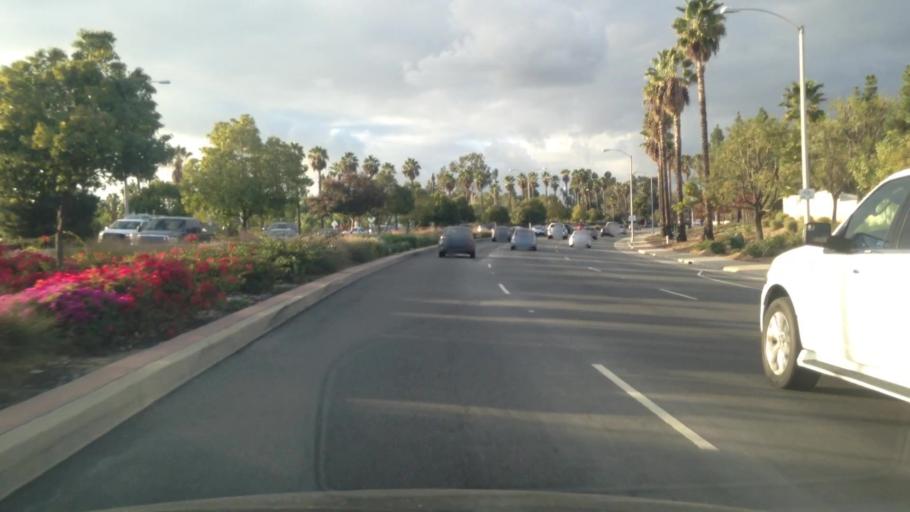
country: US
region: California
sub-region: Riverside County
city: Woodcrest
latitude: 33.9173
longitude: -117.3309
